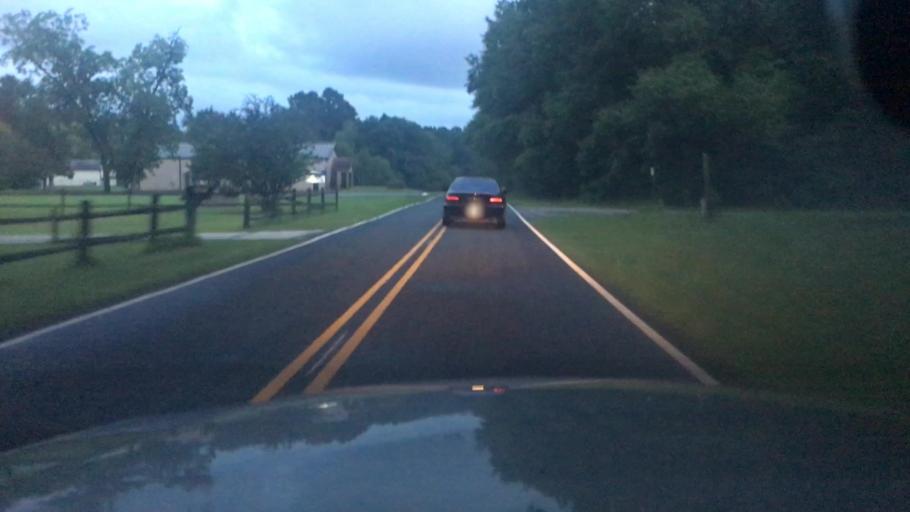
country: US
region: North Carolina
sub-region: Cumberland County
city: Hope Mills
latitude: 34.9645
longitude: -78.9266
